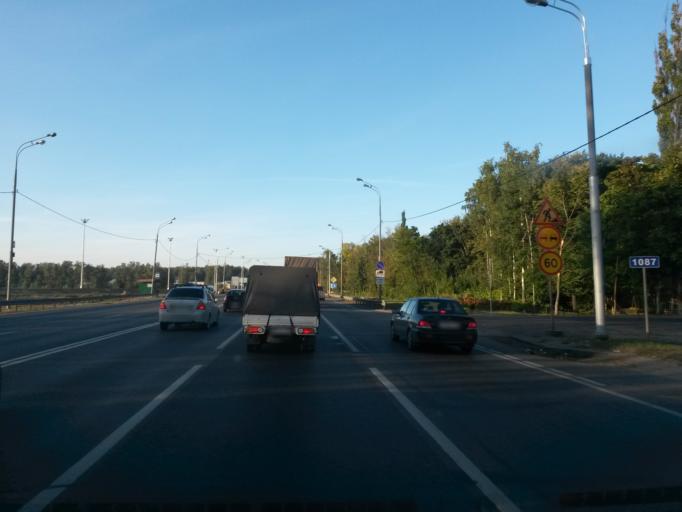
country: RU
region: Moskovskaya
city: Bolshevo
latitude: 55.9488
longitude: 37.8150
